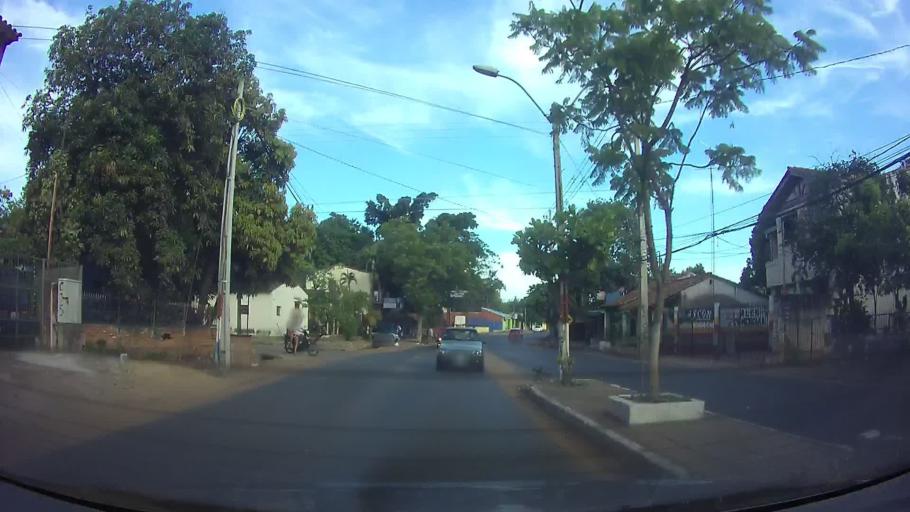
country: PY
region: Central
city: San Antonio
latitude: -25.4241
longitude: -57.5601
